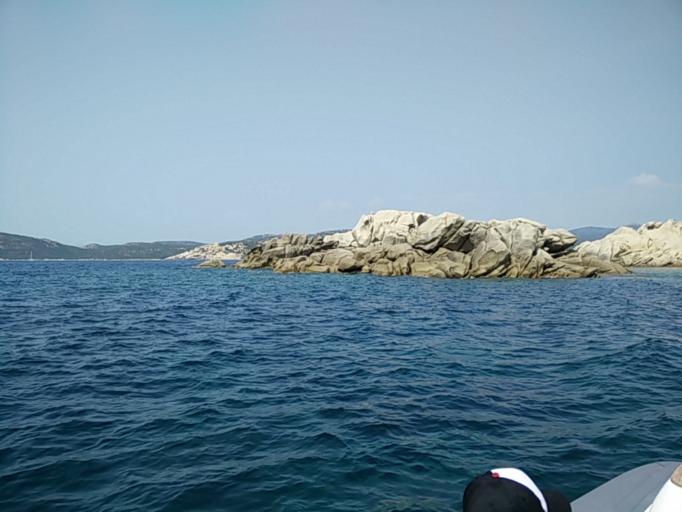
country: FR
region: Corsica
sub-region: Departement de la Corse-du-Sud
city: Propriano
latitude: 41.5661
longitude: 8.7888
